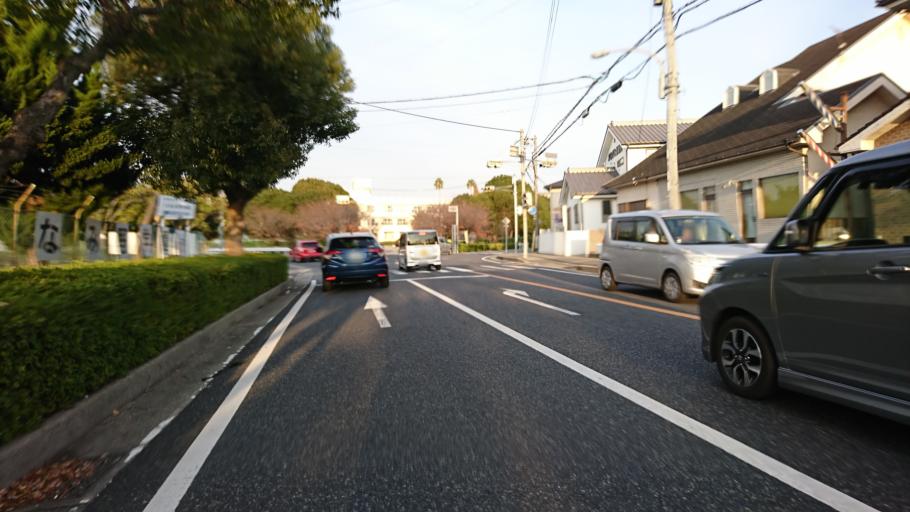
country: JP
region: Hyogo
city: Kakogawacho-honmachi
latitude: 34.7520
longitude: 134.8725
